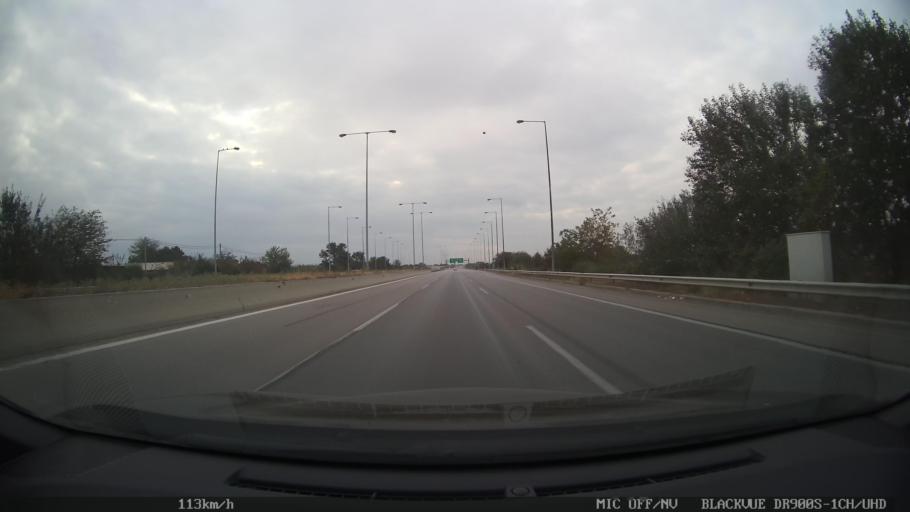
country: GR
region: Central Macedonia
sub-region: Nomos Thessalonikis
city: Kalochori
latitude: 40.6614
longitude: 22.8385
